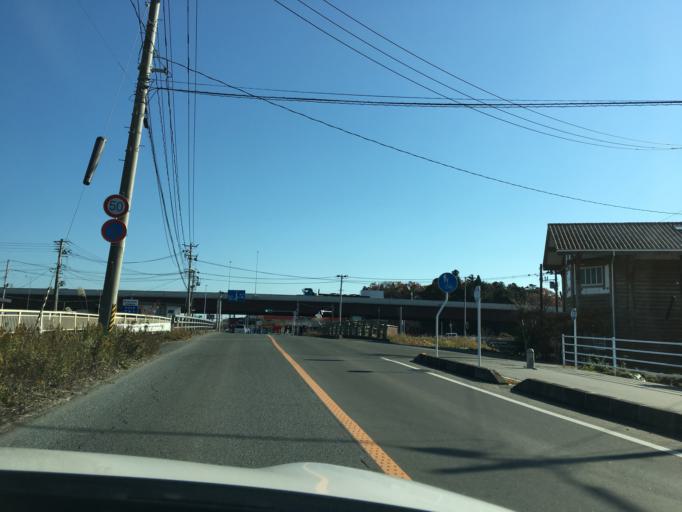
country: JP
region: Fukushima
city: Iwaki
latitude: 36.9396
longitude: 140.8549
